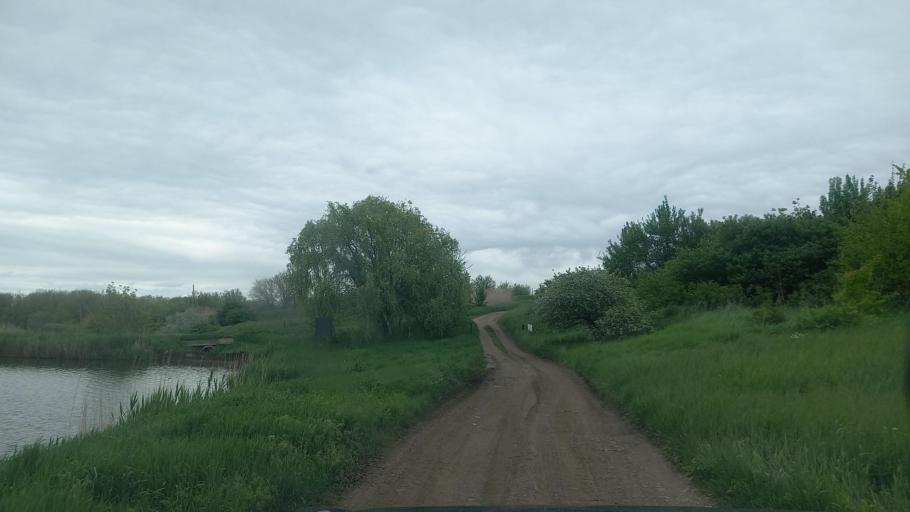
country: RU
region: Krasnodarskiy
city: Konokovo
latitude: 44.8427
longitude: 41.3470
